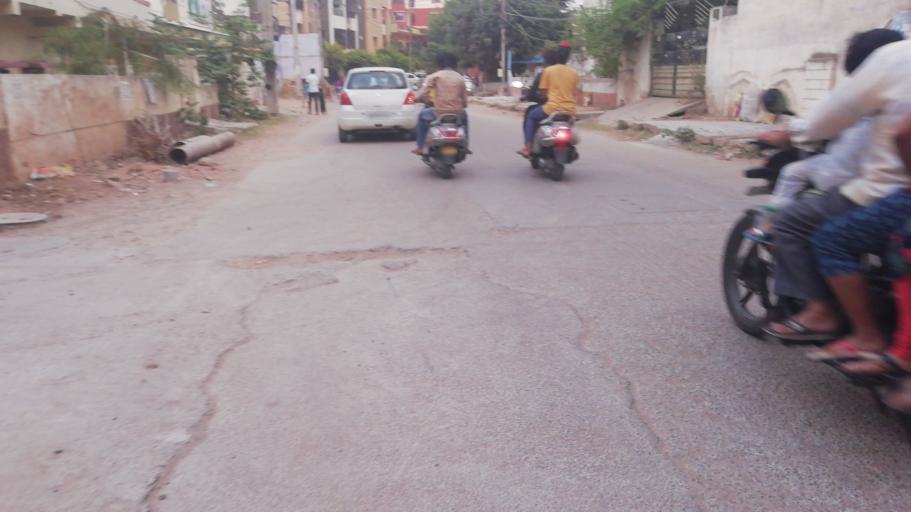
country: IN
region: Telangana
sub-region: Rangareddi
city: Gaddi Annaram
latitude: 17.3642
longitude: 78.5346
